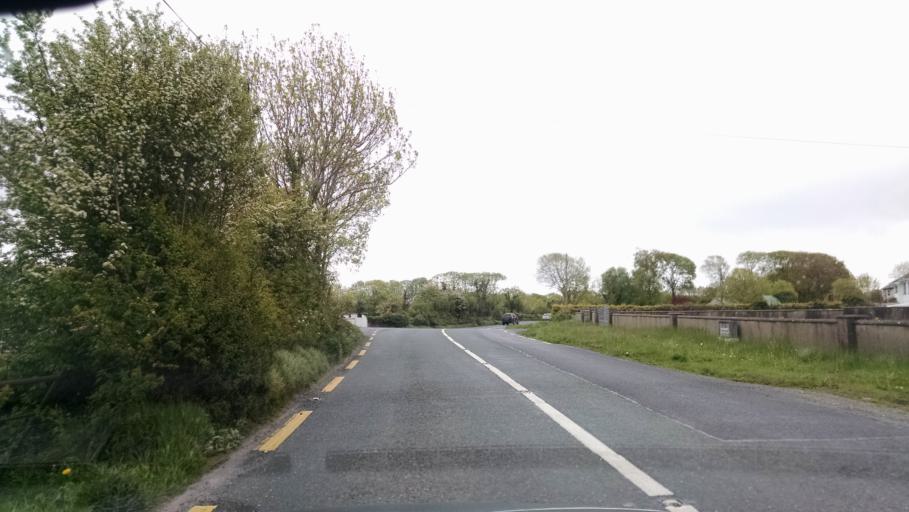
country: IE
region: Connaught
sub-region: County Galway
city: Claregalway
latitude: 53.4370
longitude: -9.0620
